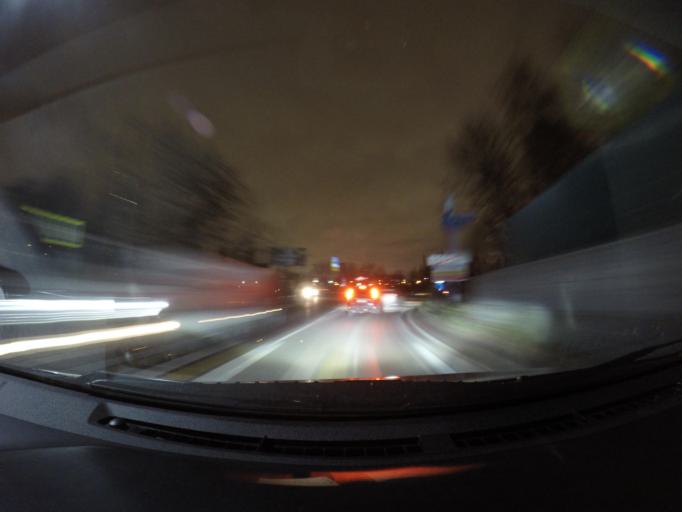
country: RU
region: Moskovskaya
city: Alekseyevka
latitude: 55.6161
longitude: 37.7877
